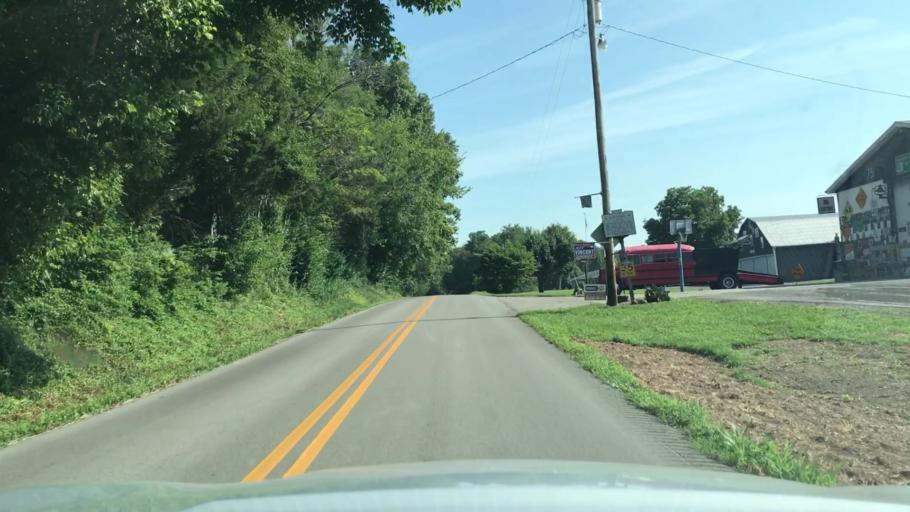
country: US
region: Kentucky
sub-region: Clinton County
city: Albany
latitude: 36.6659
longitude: -85.0723
